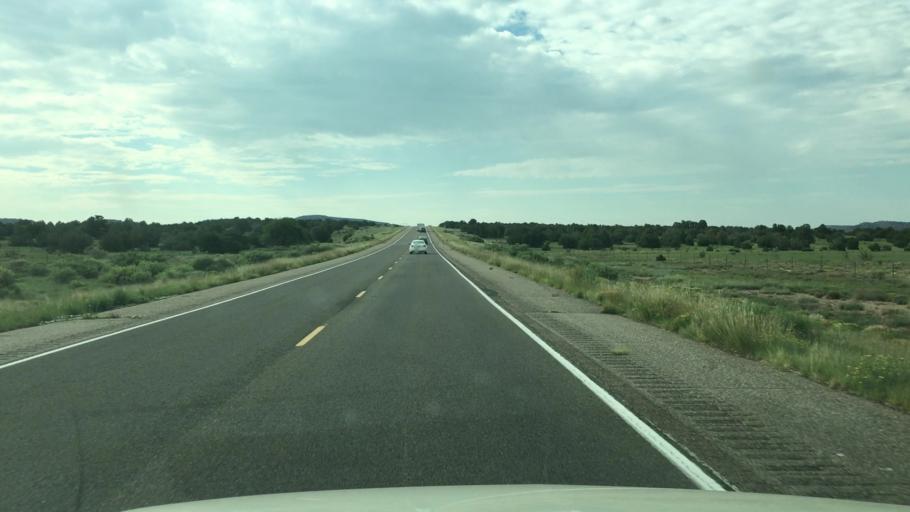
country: US
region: New Mexico
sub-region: Santa Fe County
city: Eldorado at Santa Fe
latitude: 35.3383
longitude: -105.8389
